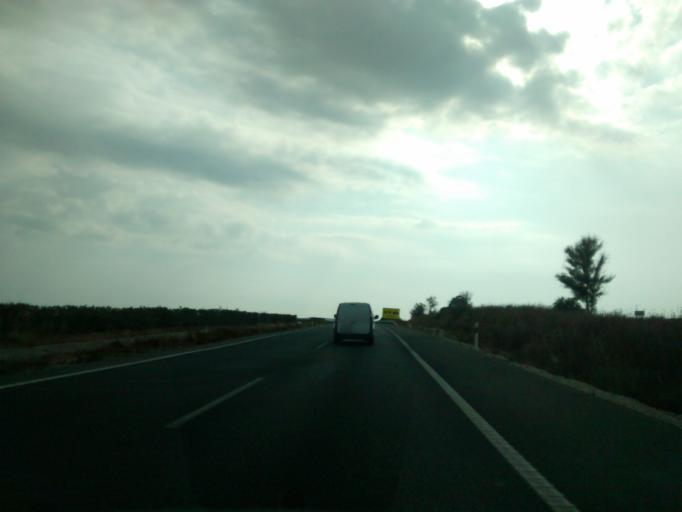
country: ES
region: Andalusia
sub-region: Provincia de Cadiz
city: Arcos de la Frontera
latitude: 36.7331
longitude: -5.8997
